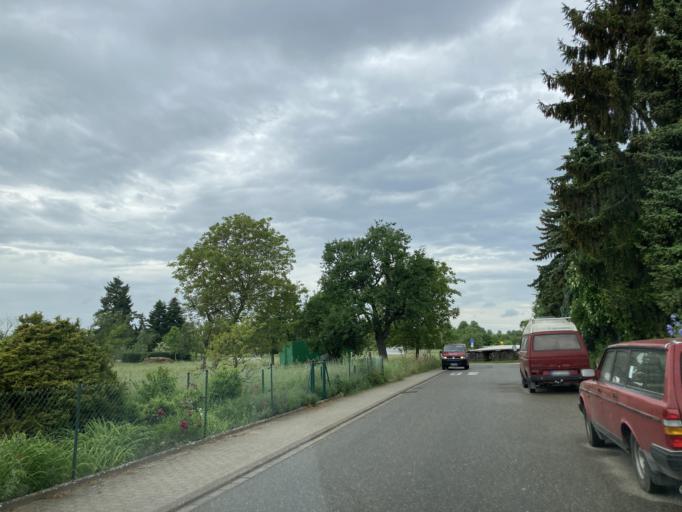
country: DE
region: Baden-Wuerttemberg
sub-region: Karlsruhe Region
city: Malsch
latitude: 48.8853
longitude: 8.3400
